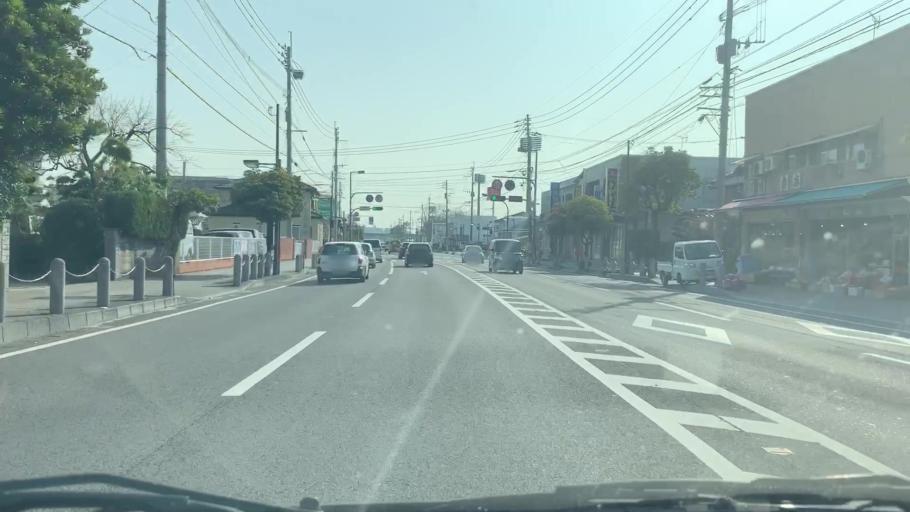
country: JP
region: Saga Prefecture
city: Saga-shi
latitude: 33.2802
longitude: 130.2922
